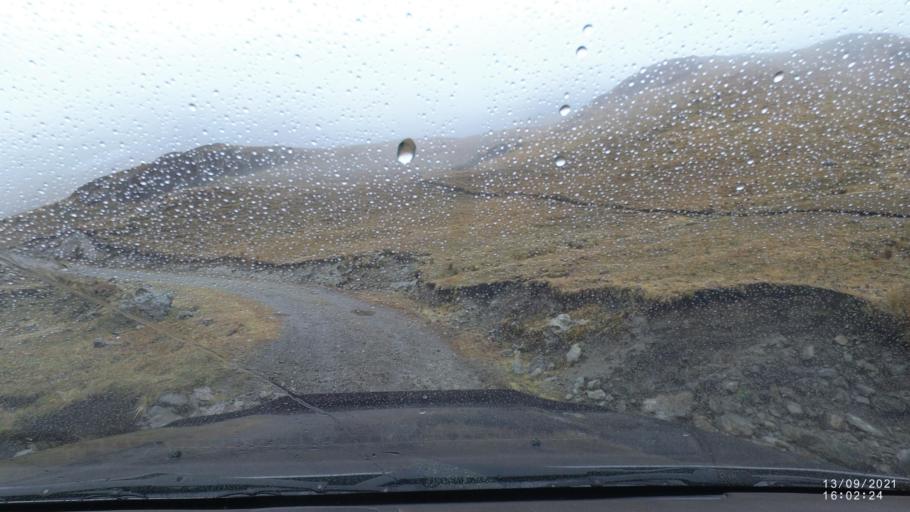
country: BO
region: Cochabamba
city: Colomi
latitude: -17.2937
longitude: -65.7093
